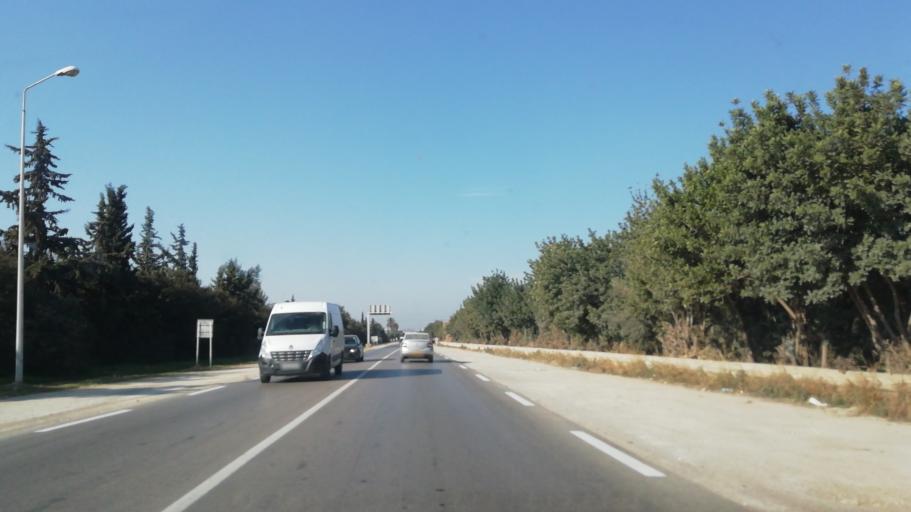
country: DZ
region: Relizane
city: Relizane
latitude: 35.7221
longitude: 0.5054
